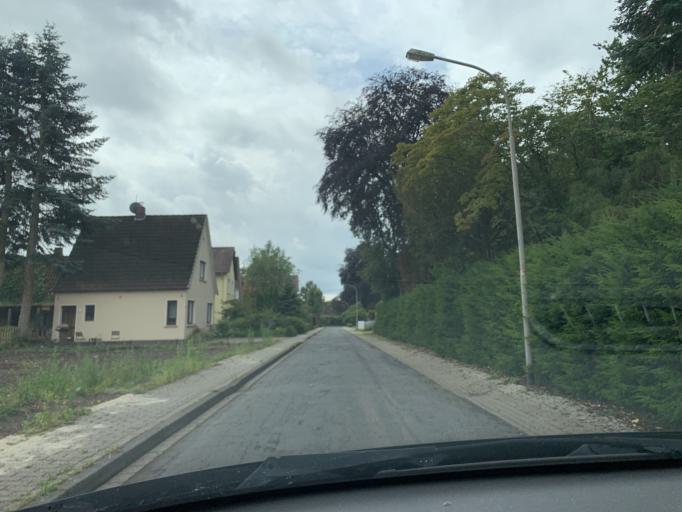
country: DE
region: Lower Saxony
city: Westerstede
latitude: 53.2529
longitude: 7.9218
